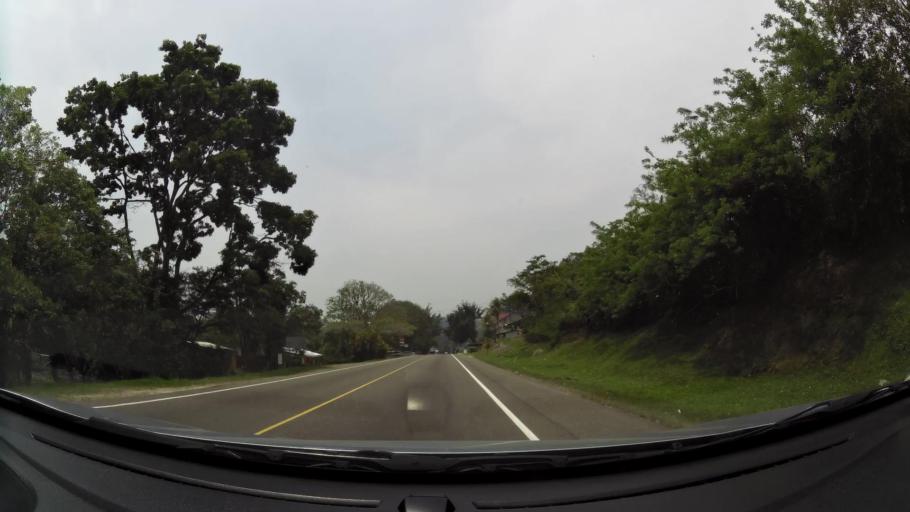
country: HN
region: Cortes
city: La Guama
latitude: 14.8605
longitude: -87.9522
